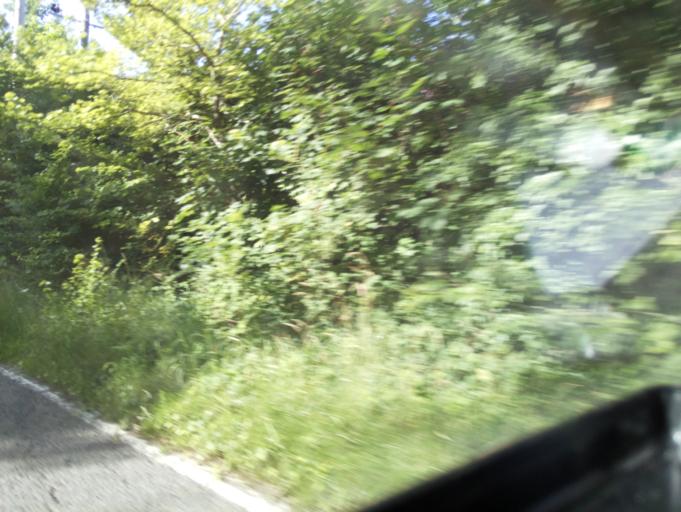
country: GB
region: England
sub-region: South Gloucestershire
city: Pucklechurch
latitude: 51.4485
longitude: -2.4175
